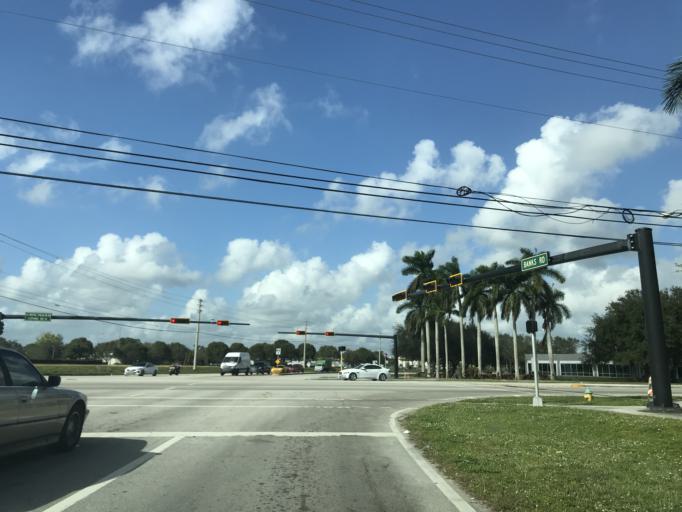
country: US
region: Florida
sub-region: Broward County
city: Margate
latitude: 26.2552
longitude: -80.1950
